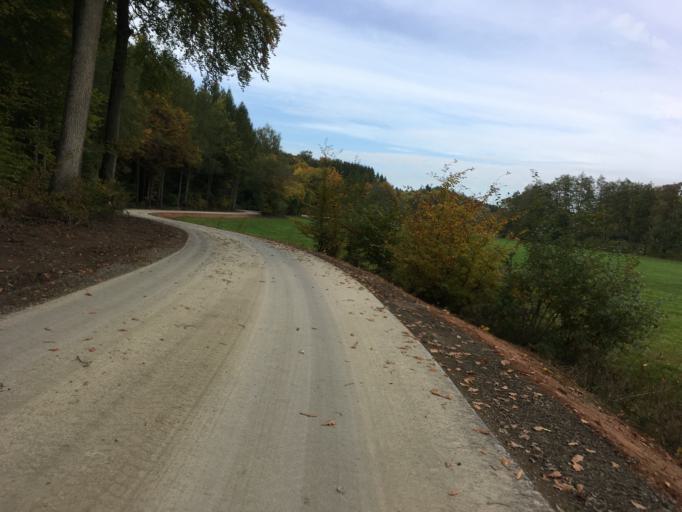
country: DE
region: Baden-Wuerttemberg
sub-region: Karlsruhe Region
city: Buchen
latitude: 49.4931
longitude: 9.3140
